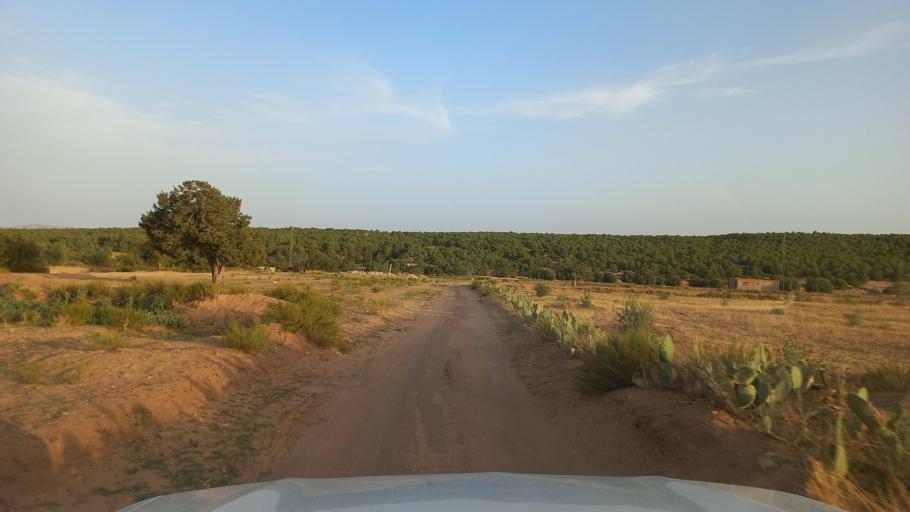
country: TN
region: Al Qasrayn
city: Sbiba
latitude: 35.4101
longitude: 8.9140
